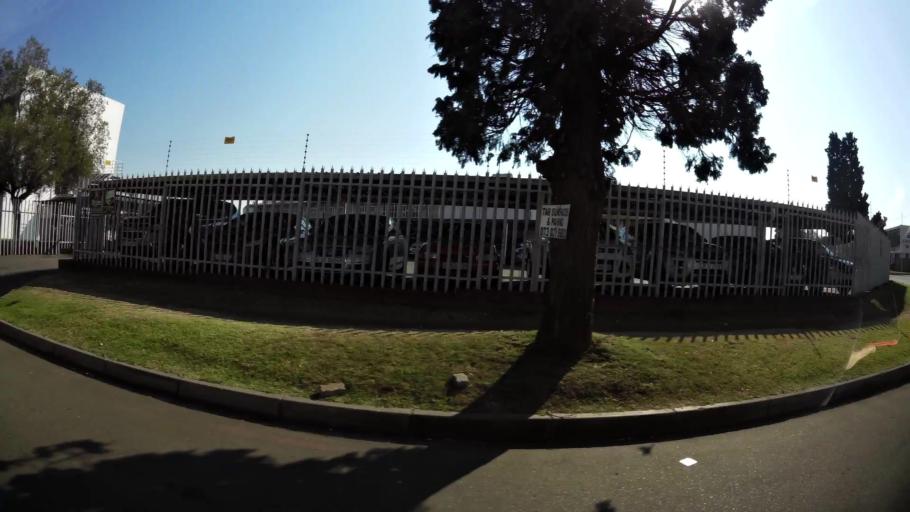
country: ZA
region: Gauteng
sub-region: City of Johannesburg Metropolitan Municipality
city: Modderfontein
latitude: -26.1483
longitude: 28.2035
